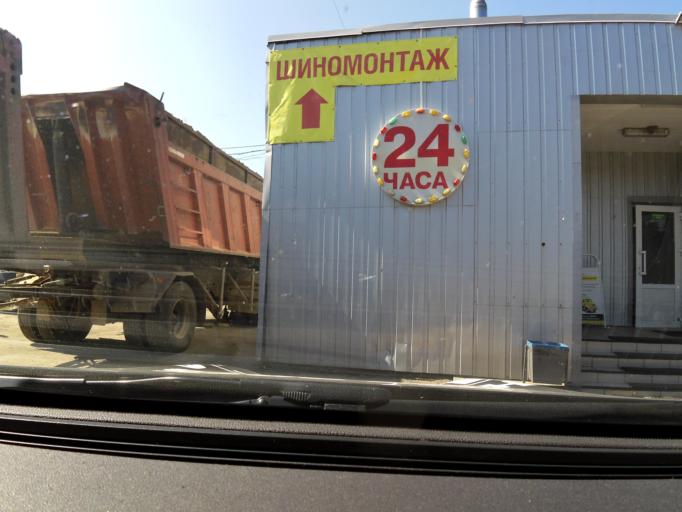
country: RU
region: Novgorod
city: Proletariy
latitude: 58.4181
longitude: 31.8390
